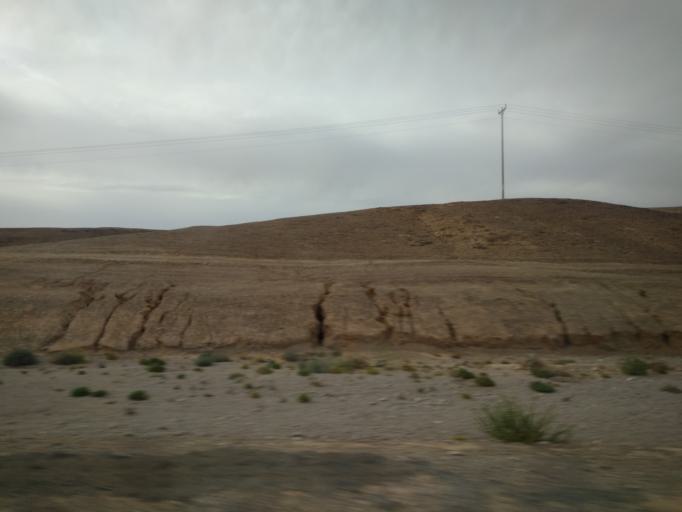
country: IL
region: Southern District
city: Eilat
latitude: 29.9358
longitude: 34.9080
